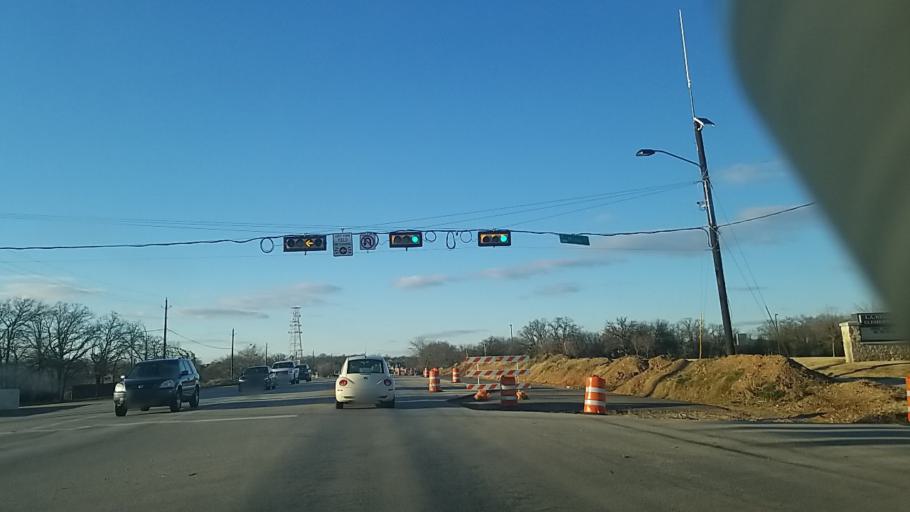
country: US
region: Texas
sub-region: Denton County
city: Corinth
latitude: 33.1616
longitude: -97.1066
